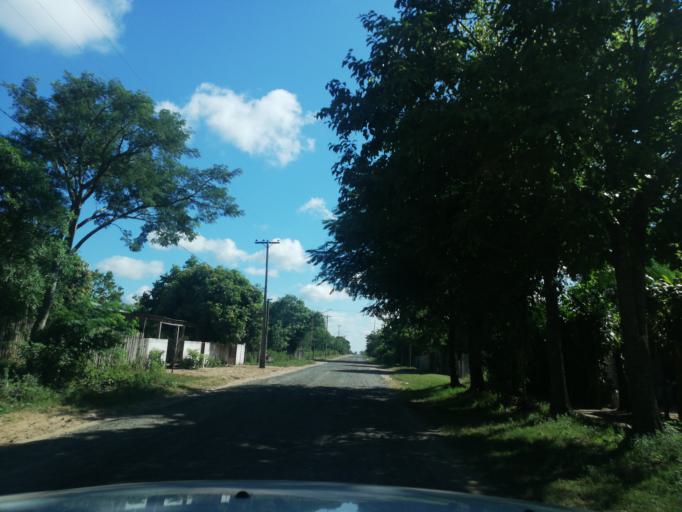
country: AR
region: Corrientes
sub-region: Departamento de San Miguel
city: San Miguel
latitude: -27.9894
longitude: -57.5872
